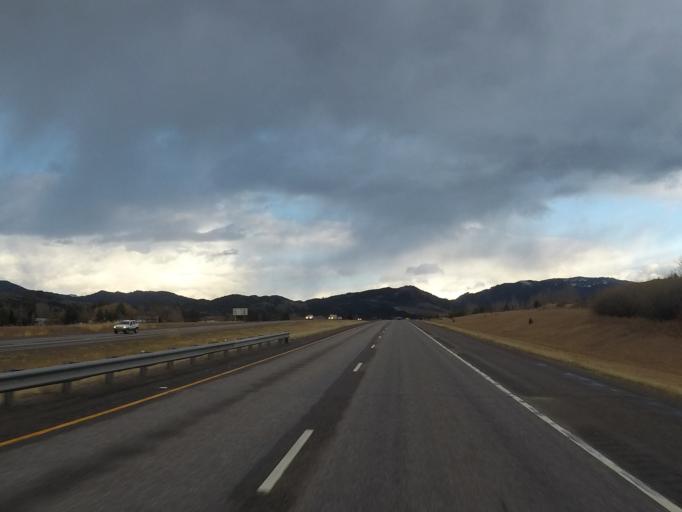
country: US
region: Montana
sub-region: Gallatin County
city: Bozeman
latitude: 45.6687
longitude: -110.9909
